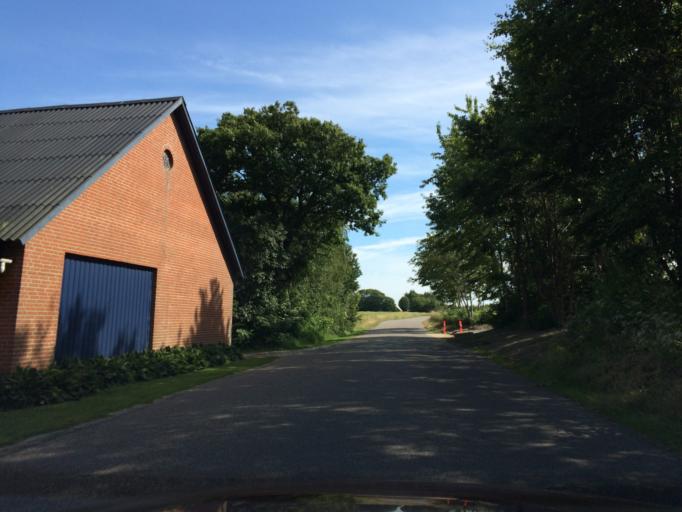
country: DK
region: Central Jutland
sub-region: Silkeborg Kommune
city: Silkeborg
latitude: 56.2182
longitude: 9.5607
